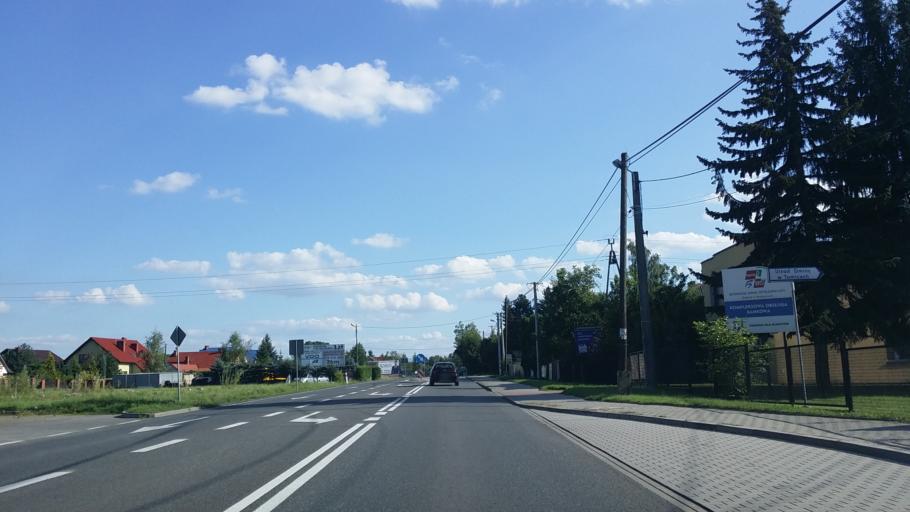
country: PL
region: Lesser Poland Voivodeship
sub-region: Powiat wadowicki
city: Tomice
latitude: 49.9004
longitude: 19.4851
